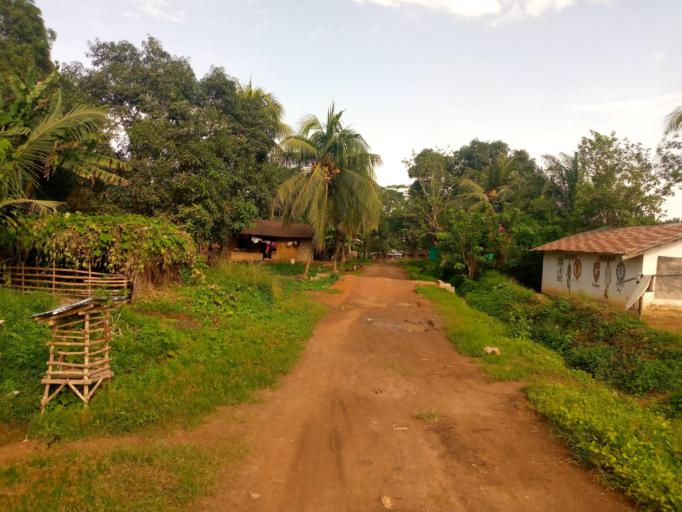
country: SL
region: Southern Province
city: Sumbuya
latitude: 7.6130
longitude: -12.1431
